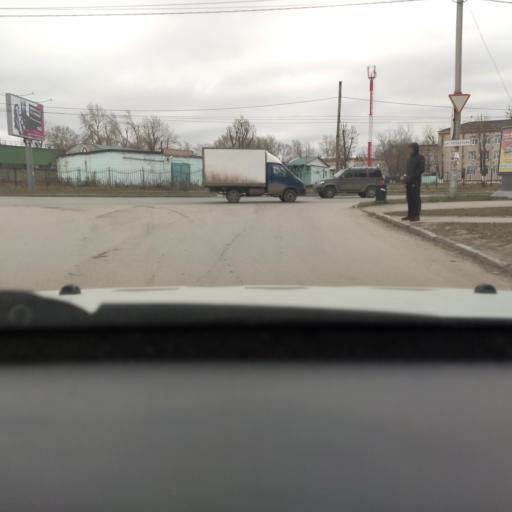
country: RU
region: Perm
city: Perm
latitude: 57.9754
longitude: 56.2431
